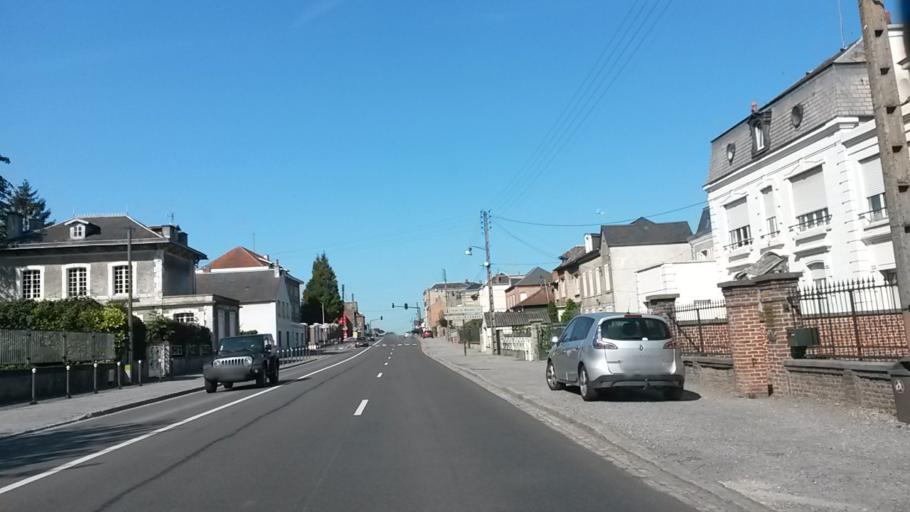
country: FR
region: Nord-Pas-de-Calais
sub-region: Departement du Nord
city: Avesnes-sur-Helpe
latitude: 50.1192
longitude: 3.9286
